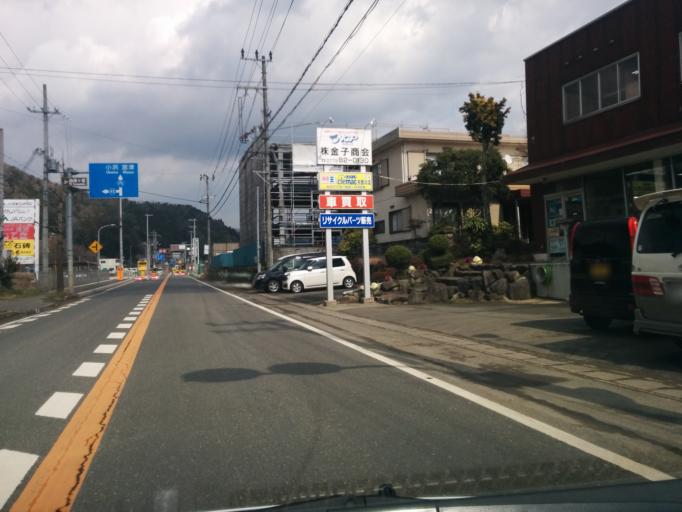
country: JP
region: Kyoto
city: Maizuru
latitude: 35.4495
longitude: 135.2632
